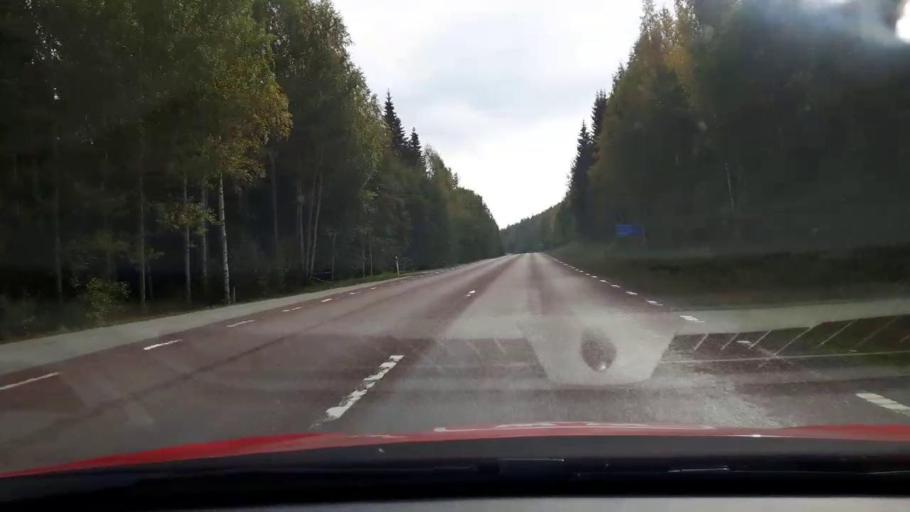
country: SE
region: Gaevleborg
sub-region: Bollnas Kommun
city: Arbra
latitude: 61.5668
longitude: 16.3310
